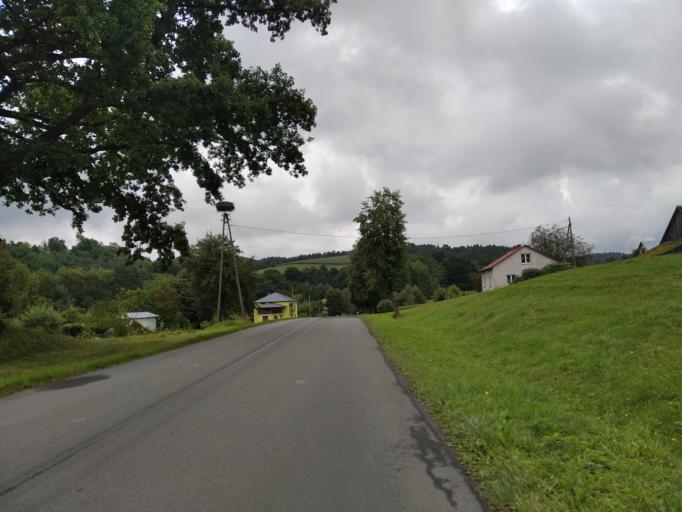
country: PL
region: Subcarpathian Voivodeship
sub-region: Powiat brzozowski
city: Nozdrzec
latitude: 49.7243
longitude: 22.2891
